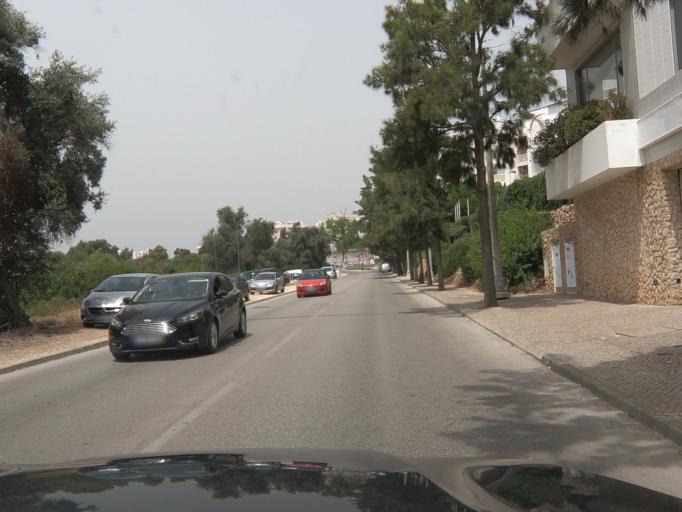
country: PT
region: Faro
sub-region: Portimao
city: Portimao
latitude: 37.1236
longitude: -8.5413
